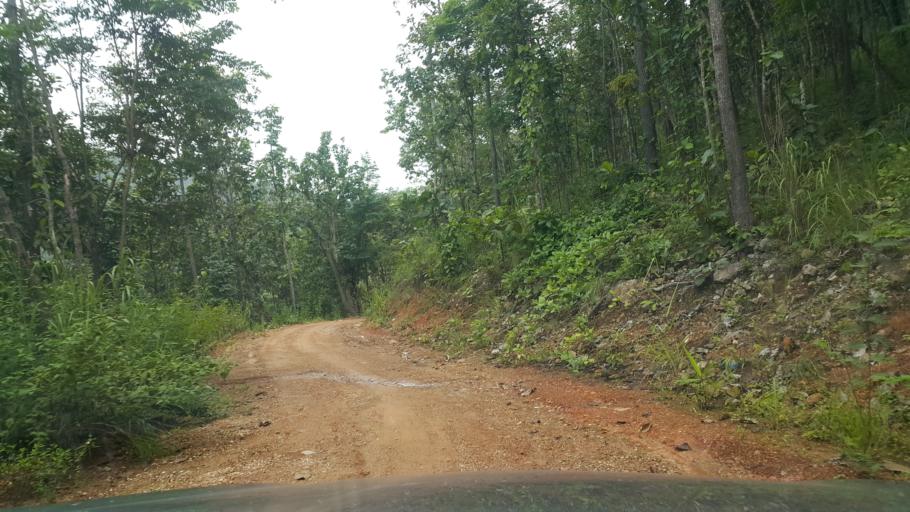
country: TH
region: Chiang Mai
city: San Sai
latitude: 18.9573
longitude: 99.1312
